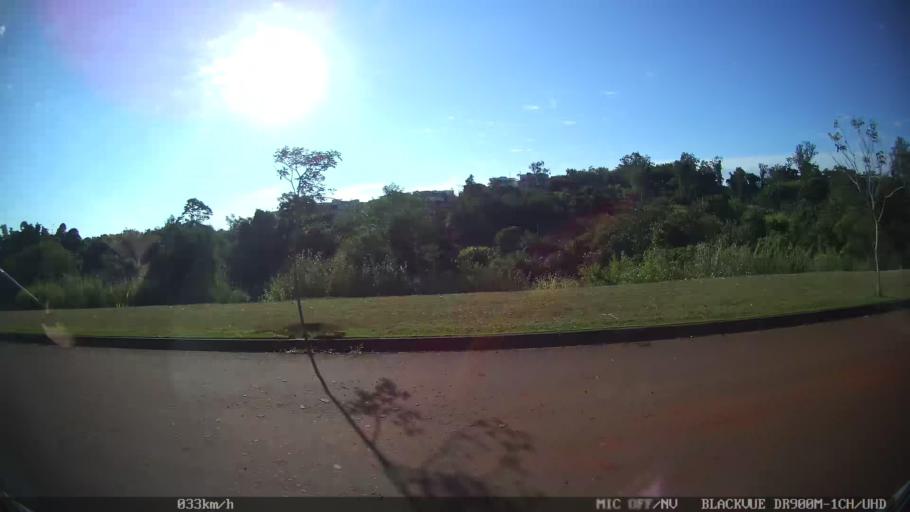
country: BR
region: Sao Paulo
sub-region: Piracicaba
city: Piracicaba
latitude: -22.6912
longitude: -47.6243
